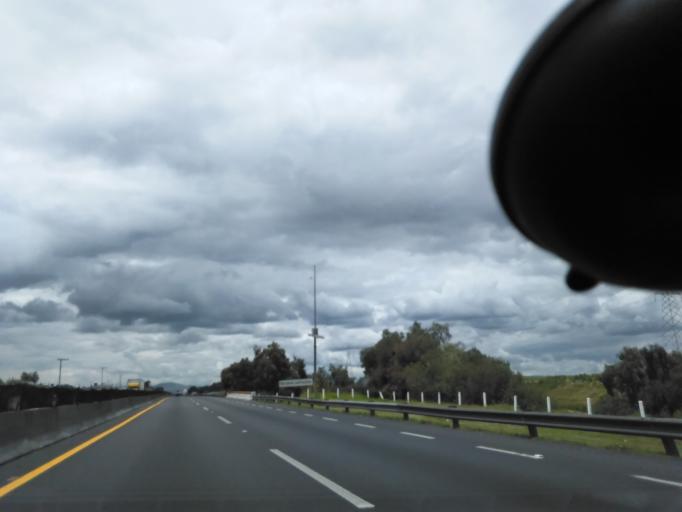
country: MX
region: Mexico
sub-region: Jaltenco
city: Alborada Jaltenco
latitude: 19.6533
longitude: -99.0603
